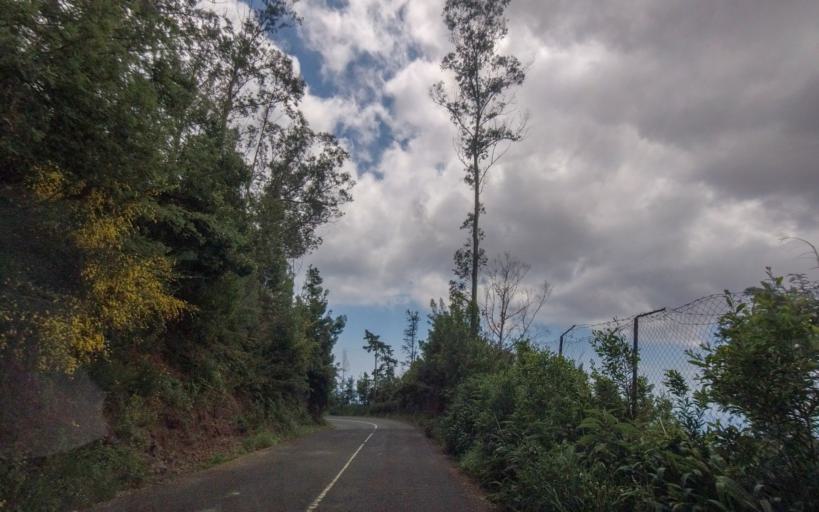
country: PT
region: Madeira
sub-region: Funchal
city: Nossa Senhora do Monte
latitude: 32.6745
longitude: -16.8846
